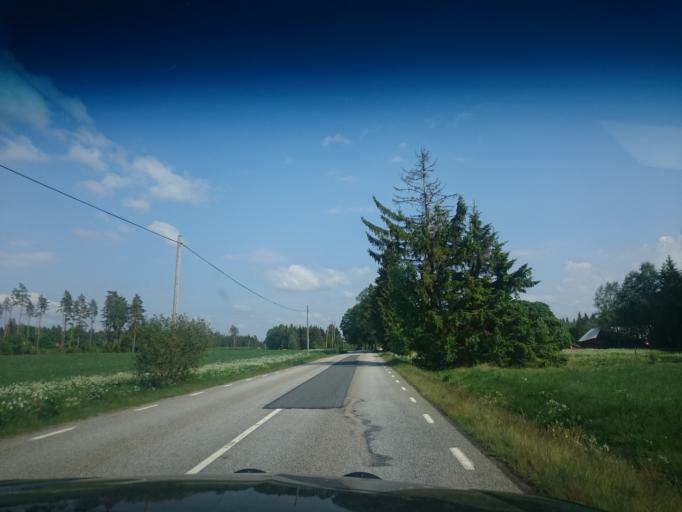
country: SE
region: Joenkoeping
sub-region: Vetlanda Kommun
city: Landsbro
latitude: 57.3802
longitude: 14.9863
